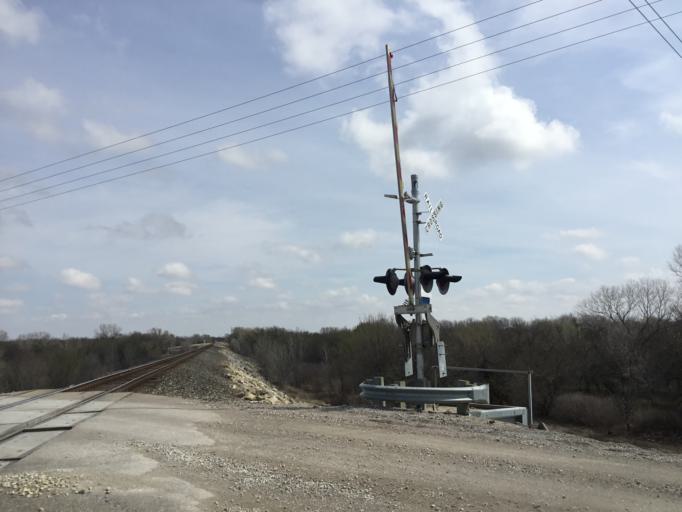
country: US
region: Kansas
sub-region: Butler County
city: Rose Hill
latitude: 37.5882
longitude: -97.0987
